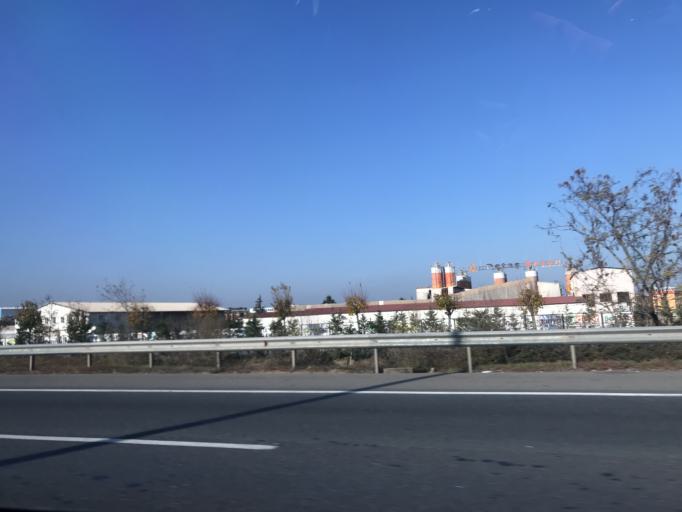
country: TR
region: Istanbul
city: Samandira
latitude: 40.9824
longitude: 29.2089
